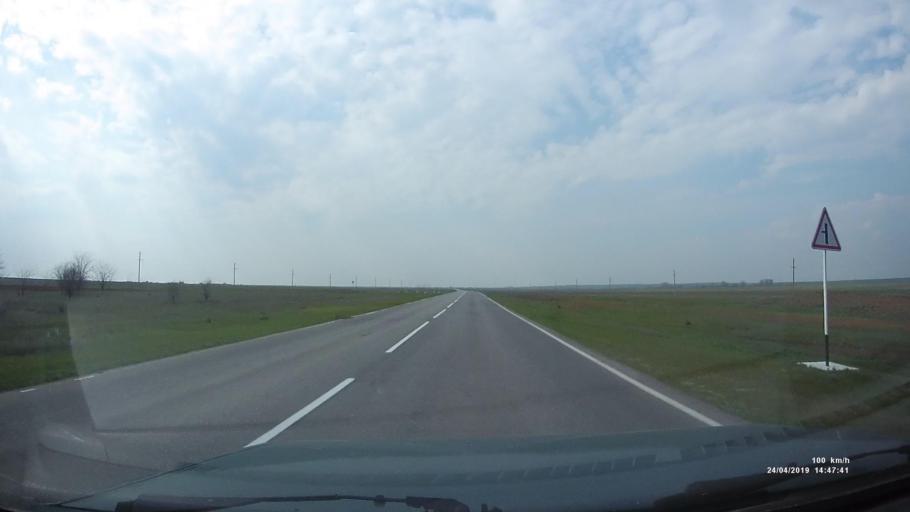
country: RU
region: Rostov
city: Remontnoye
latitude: 46.4939
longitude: 43.7687
